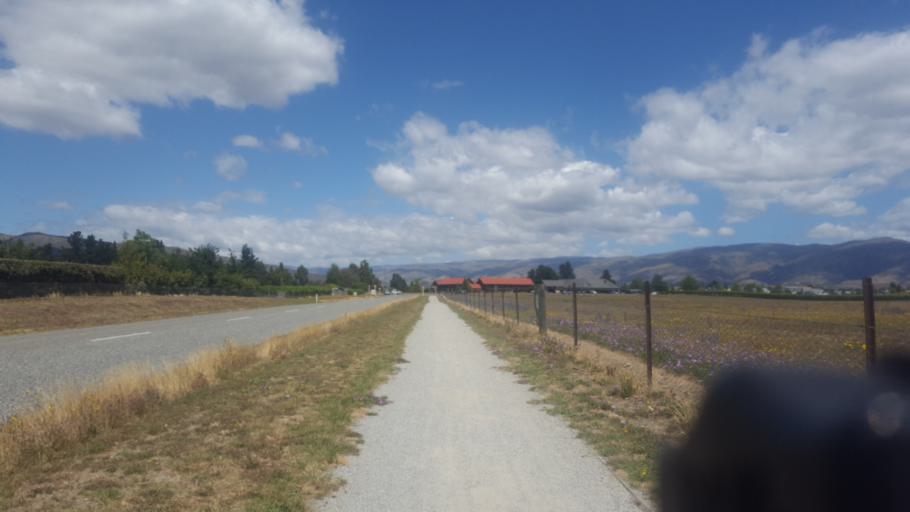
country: NZ
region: Otago
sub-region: Queenstown-Lakes District
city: Wanaka
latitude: -45.0324
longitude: 169.2029
